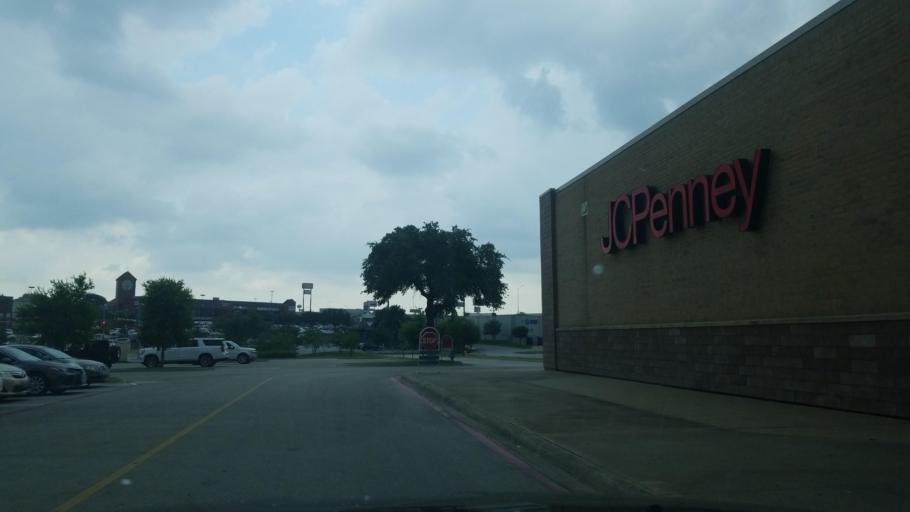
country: US
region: Texas
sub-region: Denton County
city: Denton
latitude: 33.1894
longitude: -97.1074
